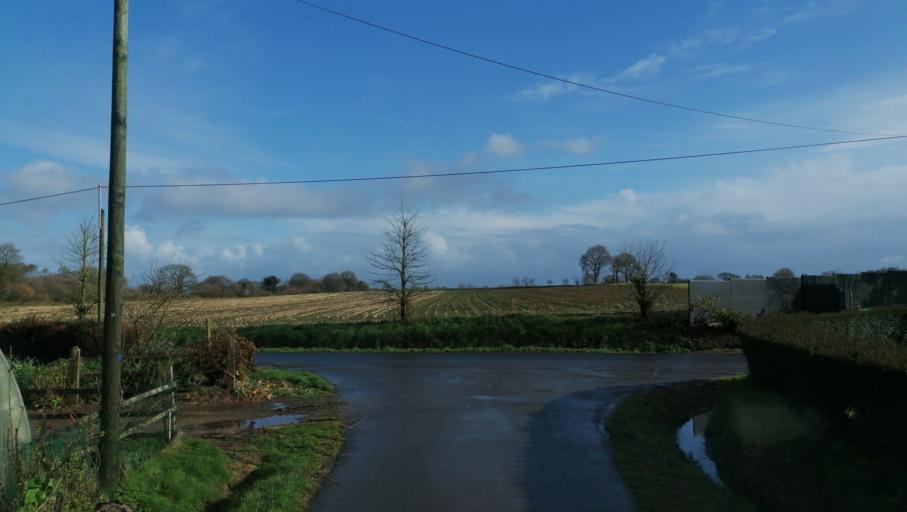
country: FR
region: Brittany
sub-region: Departement des Cotes-d'Armor
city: Lanrodec
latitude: 48.4950
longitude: -3.0125
